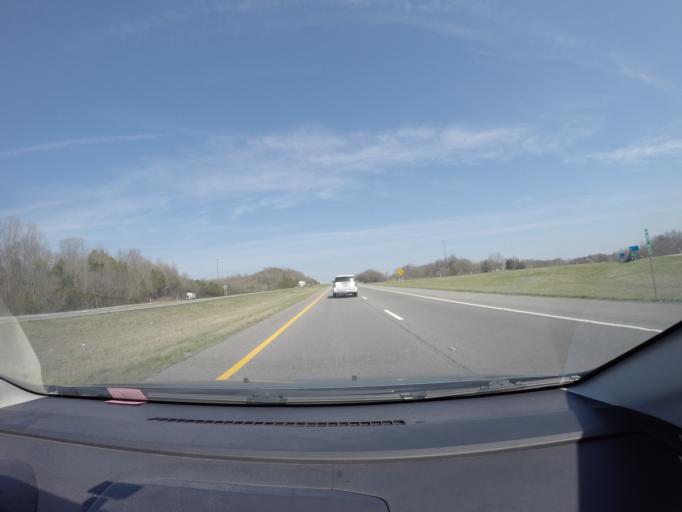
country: US
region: Tennessee
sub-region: Rutherford County
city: Plainview
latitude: 35.6233
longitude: -86.2423
